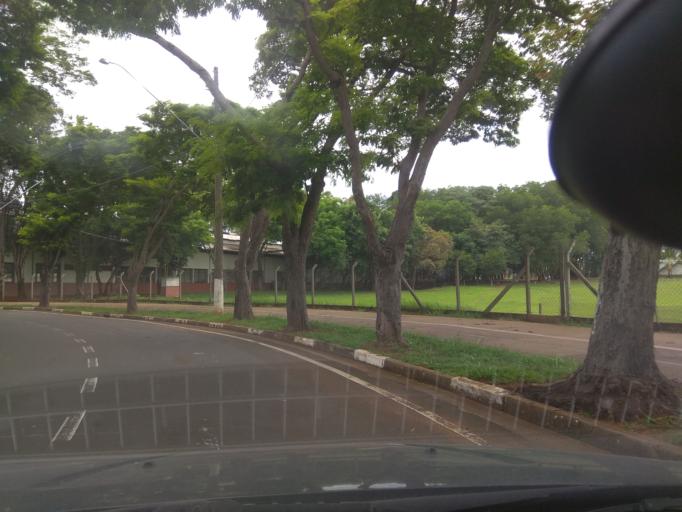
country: BR
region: Sao Paulo
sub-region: Campinas
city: Campinas
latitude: -22.8184
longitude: -47.0724
